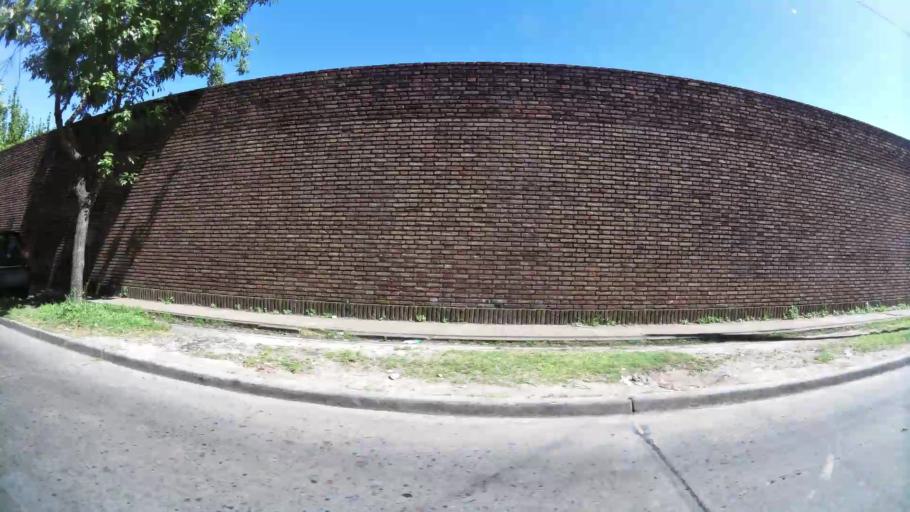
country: AR
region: Buenos Aires
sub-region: Partido de Vicente Lopez
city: Olivos
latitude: -34.5178
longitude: -58.5235
